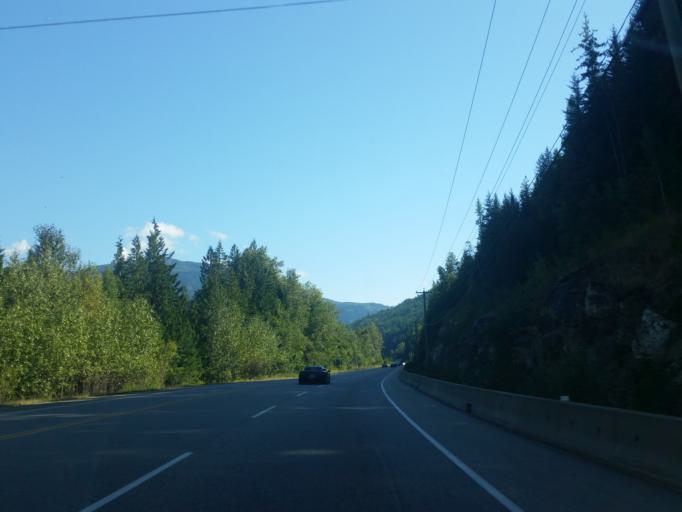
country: CA
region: British Columbia
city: Sicamous
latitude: 50.8561
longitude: -118.9426
